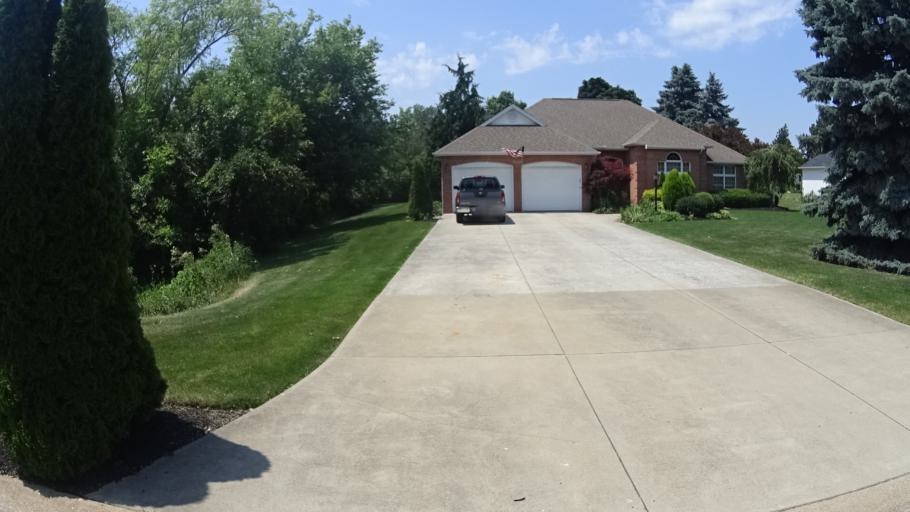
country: US
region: Ohio
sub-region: Erie County
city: Huron
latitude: 41.4116
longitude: -82.6209
